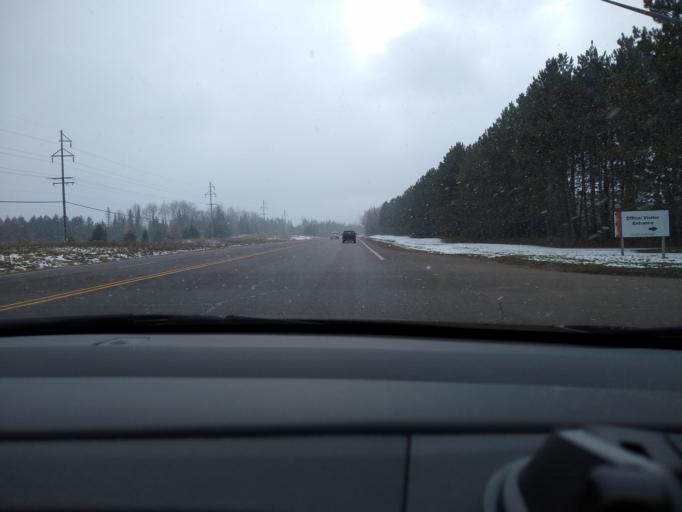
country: US
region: Michigan
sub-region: Dickinson County
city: Iron Mountain
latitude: 46.0387
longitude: -88.0609
